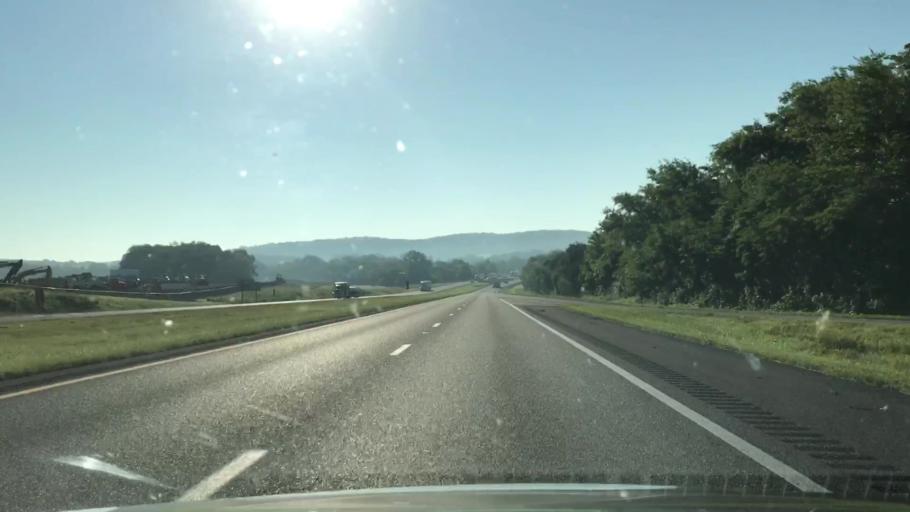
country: US
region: Tennessee
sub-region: Wilson County
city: Watertown
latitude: 36.1899
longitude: -86.1746
